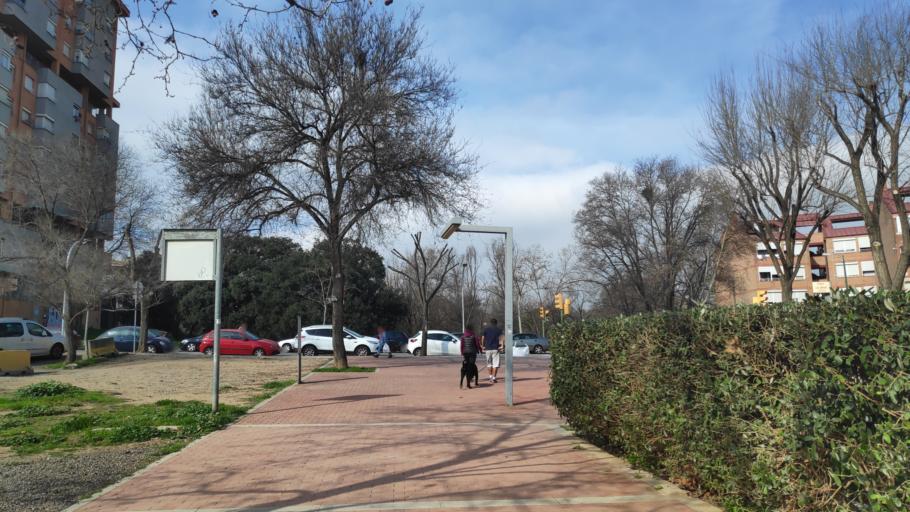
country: ES
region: Catalonia
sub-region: Provincia de Barcelona
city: Sant Quirze del Valles
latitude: 41.5532
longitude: 2.0842
